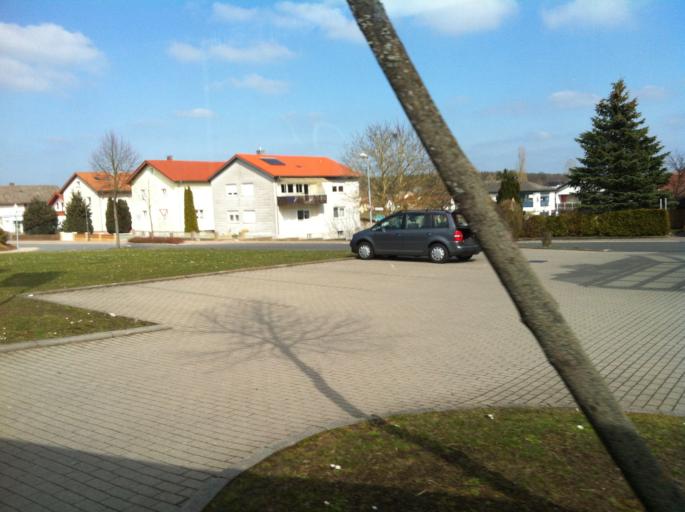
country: DE
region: Baden-Wuerttemberg
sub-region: Karlsruhe Region
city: Mudau
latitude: 49.5288
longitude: 9.2044
